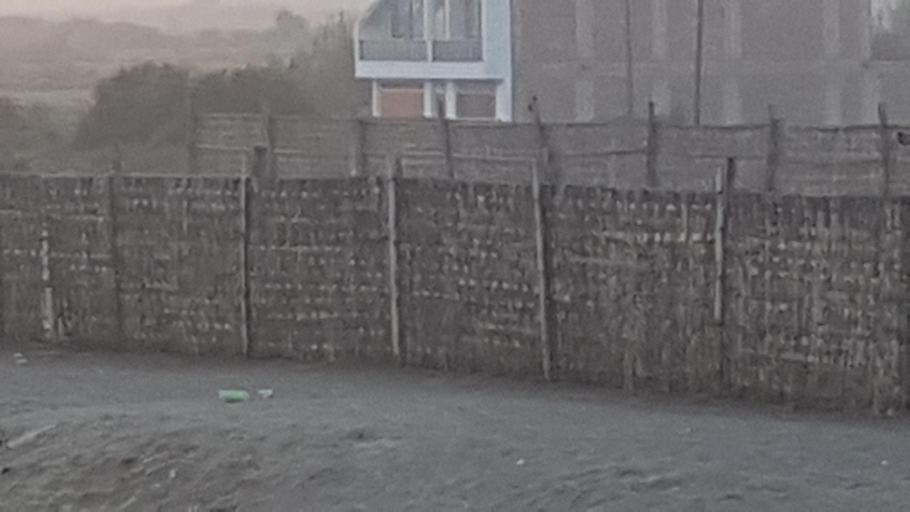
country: PE
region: Arequipa
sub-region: Provincia de Islay
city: Punta de Bombon
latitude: -17.1917
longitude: -71.7808
